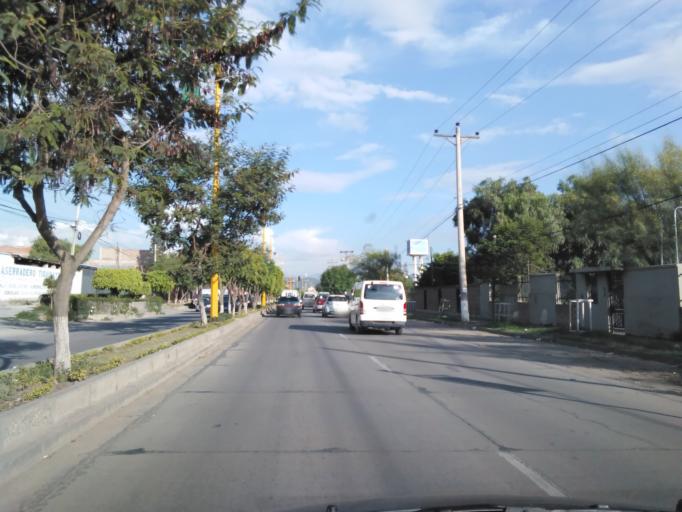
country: BO
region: Cochabamba
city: Cochabamba
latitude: -17.3499
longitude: -66.1944
